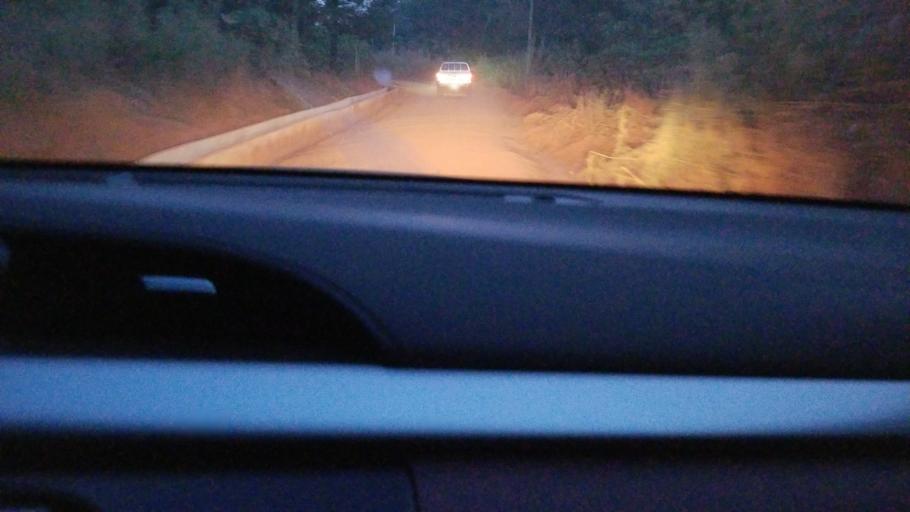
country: NG
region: Enugu
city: Obollo-Afor
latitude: 6.9031
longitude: 7.5101
